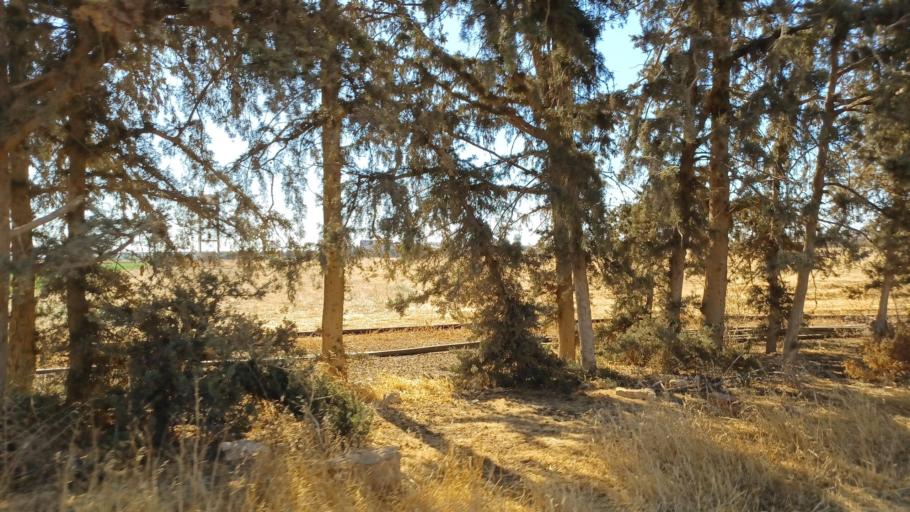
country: CY
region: Larnaka
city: Pergamos
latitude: 35.0521
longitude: 33.7048
